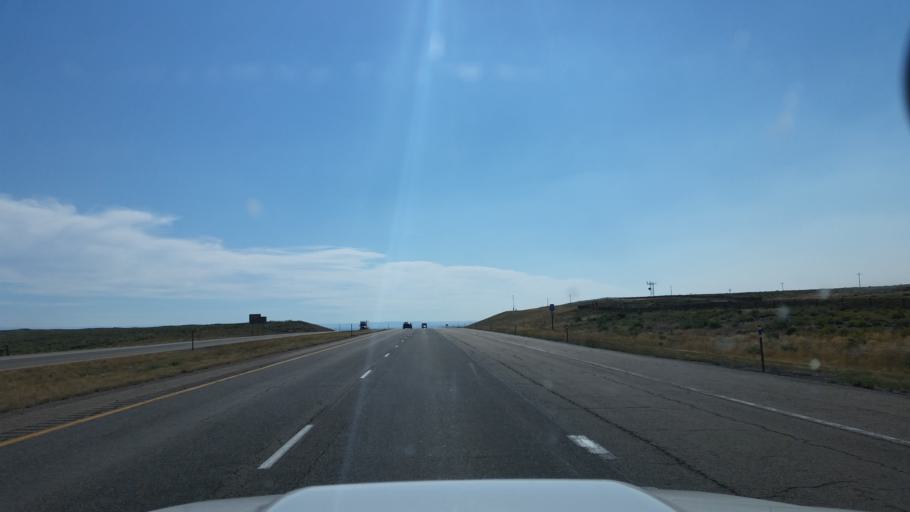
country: US
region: Wyoming
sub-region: Uinta County
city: Lyman
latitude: 41.4316
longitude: -110.1136
